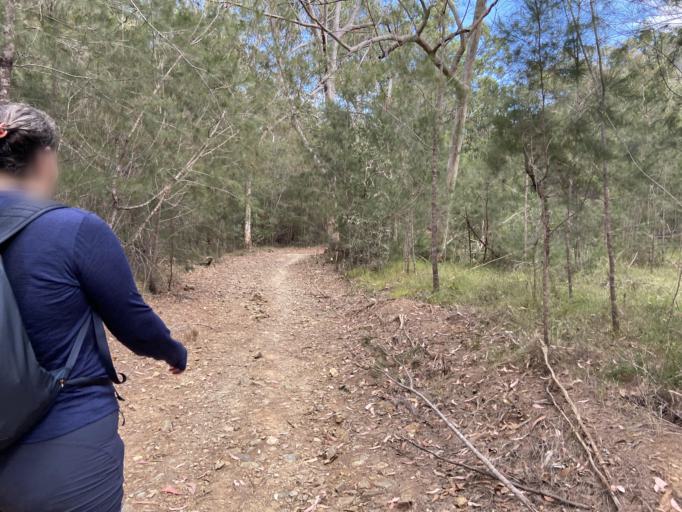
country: AU
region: Queensland
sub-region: Moreton Bay
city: Caboolture
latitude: -26.9496
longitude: 152.9560
